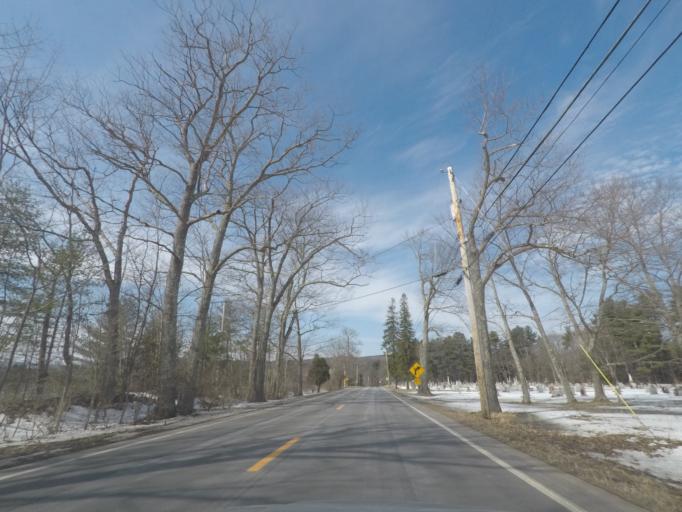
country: US
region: Massachusetts
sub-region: Berkshire County
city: West Stockbridge
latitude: 42.3493
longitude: -73.3831
